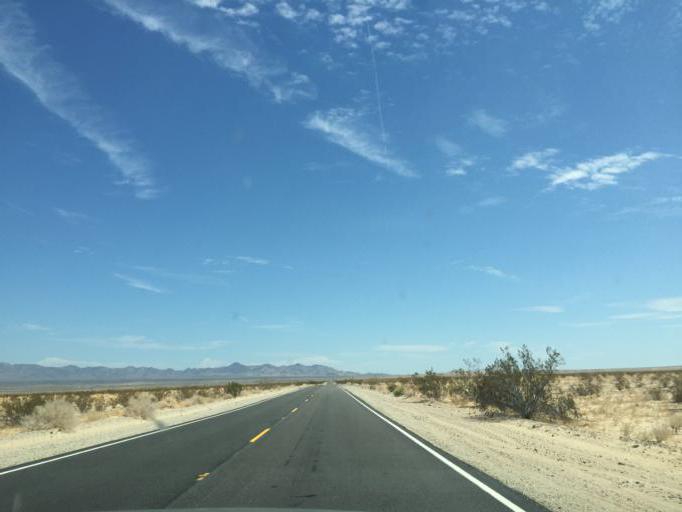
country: US
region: California
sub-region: Riverside County
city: Mesa Verde
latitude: 34.0975
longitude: -115.0242
